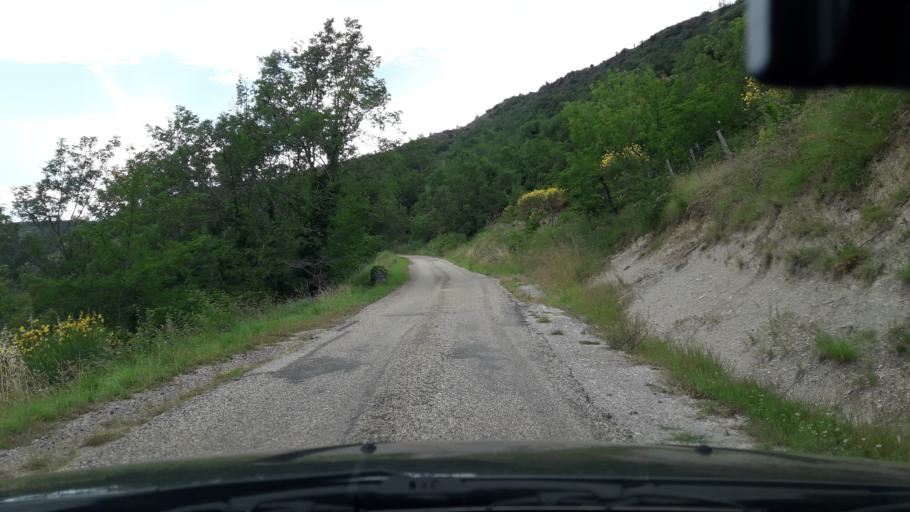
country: FR
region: Rhone-Alpes
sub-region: Departement de l'Ardeche
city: Alissas
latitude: 44.6795
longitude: 4.5985
